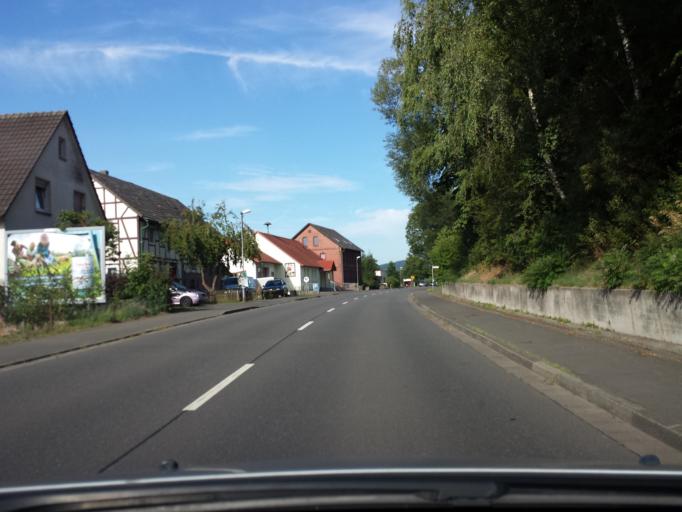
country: DE
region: Hesse
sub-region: Regierungsbezirk Kassel
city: Oberaula
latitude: 50.8566
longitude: 9.5134
